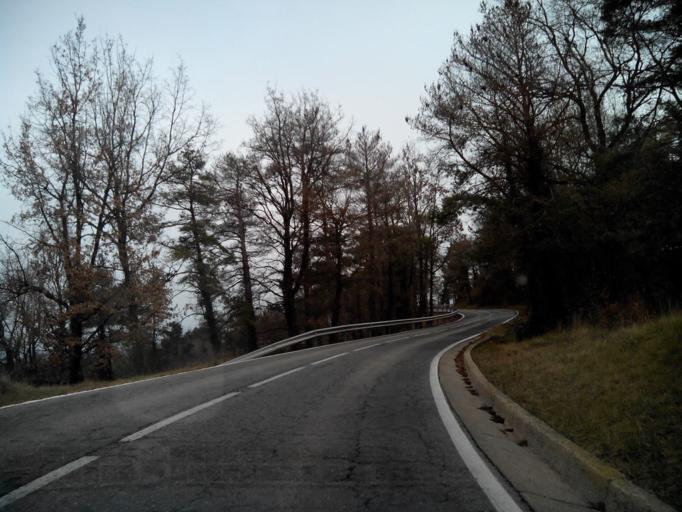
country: ES
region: Catalonia
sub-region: Provincia de Barcelona
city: Olost
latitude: 41.9676
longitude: 2.1379
